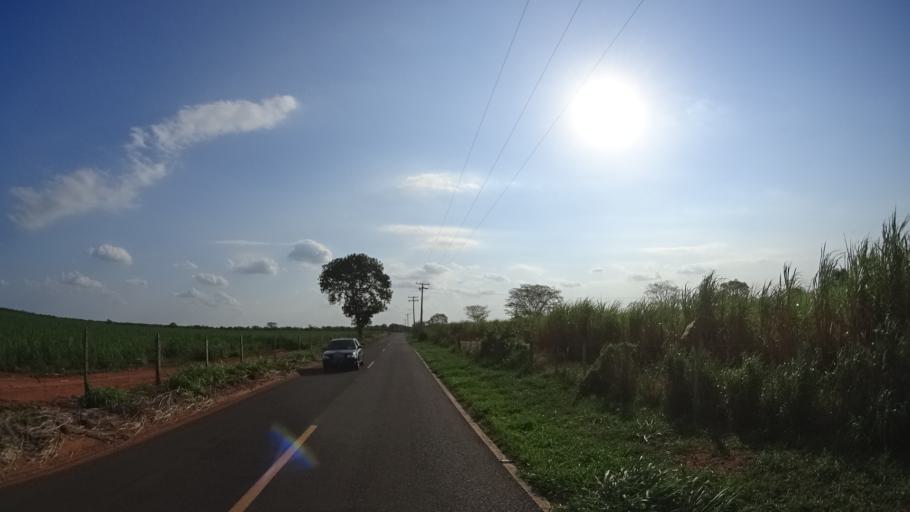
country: BR
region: Sao Paulo
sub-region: Urupes
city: Urupes
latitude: -21.3903
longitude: -49.5032
